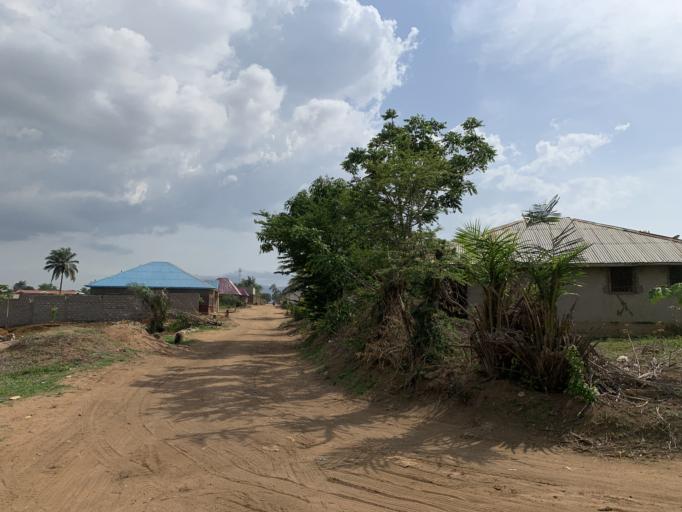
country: SL
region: Western Area
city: Waterloo
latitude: 8.3494
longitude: -13.0364
